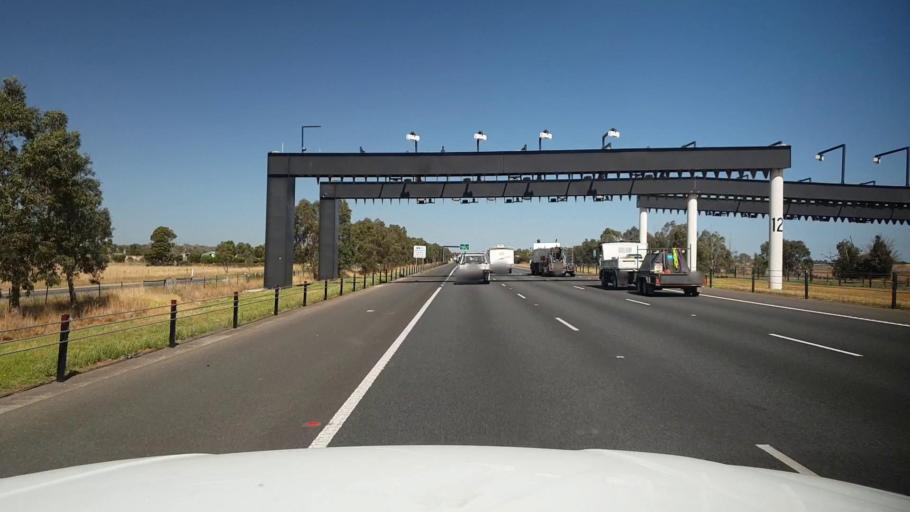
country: AU
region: Victoria
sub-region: Frankston
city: Sandhurst
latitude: -38.0539
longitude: 145.1852
